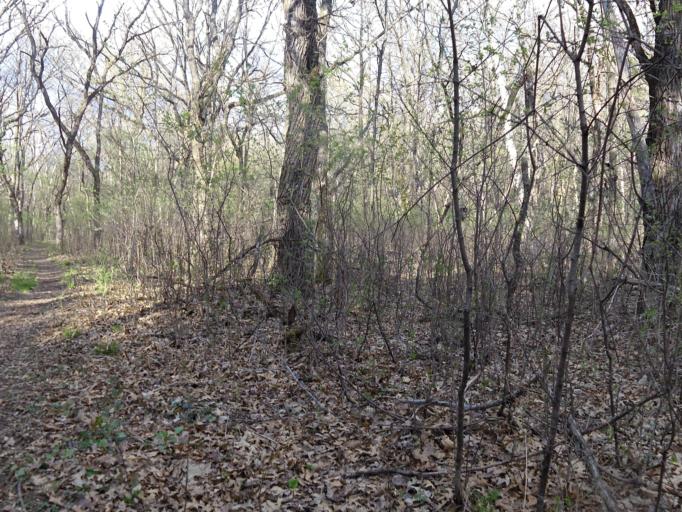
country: US
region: Wisconsin
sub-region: Saint Croix County
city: North Hudson
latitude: 45.0178
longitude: -92.6805
